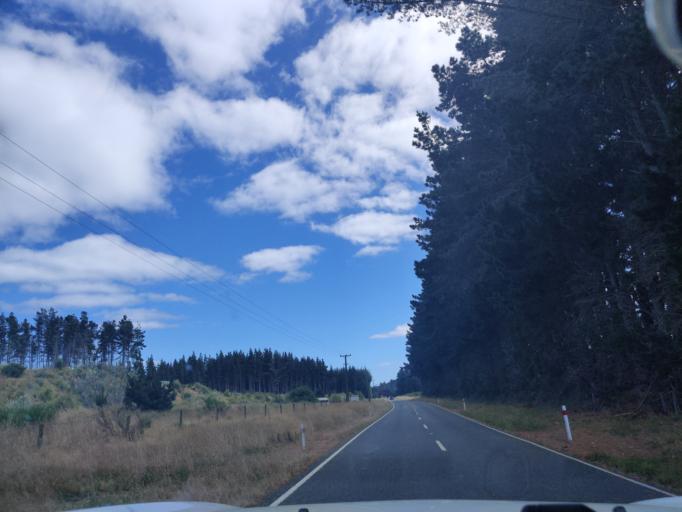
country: NZ
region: Manawatu-Wanganui
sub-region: Horowhenua District
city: Foxton
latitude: -40.3781
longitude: 175.2551
